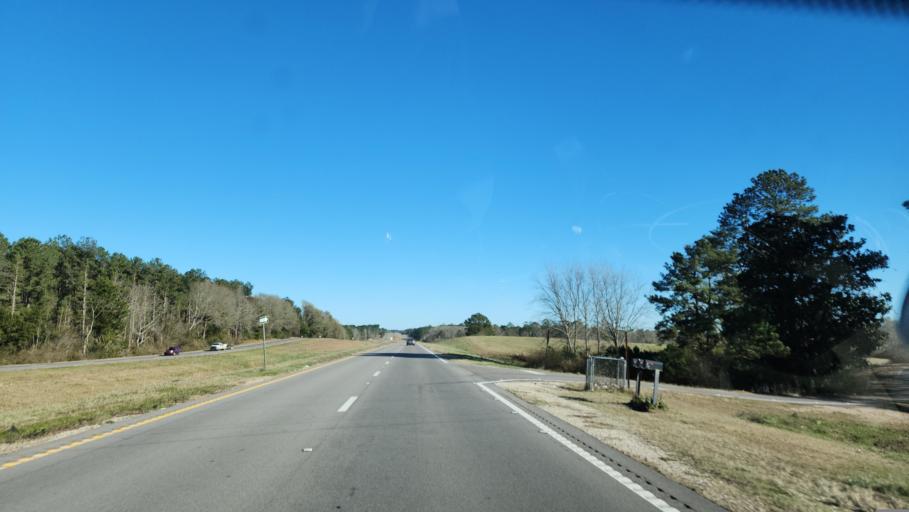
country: US
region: Mississippi
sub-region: Wayne County
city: Waynesboro
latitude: 31.6965
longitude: -88.8575
